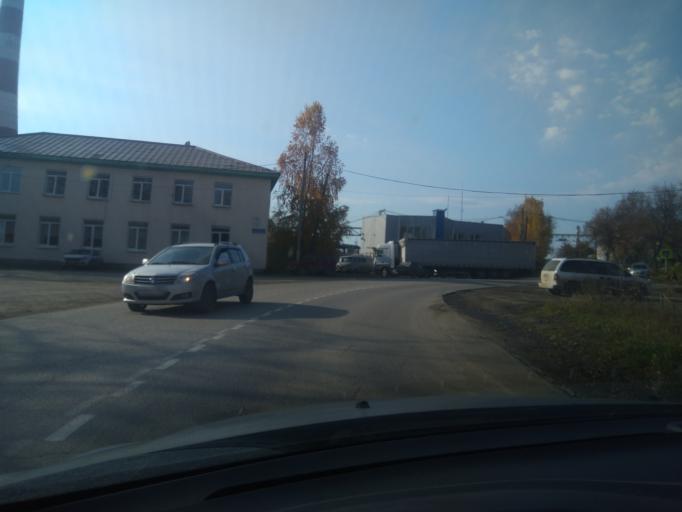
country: RU
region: Sverdlovsk
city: Nizhniye Sergi
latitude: 56.6688
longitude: 59.3197
